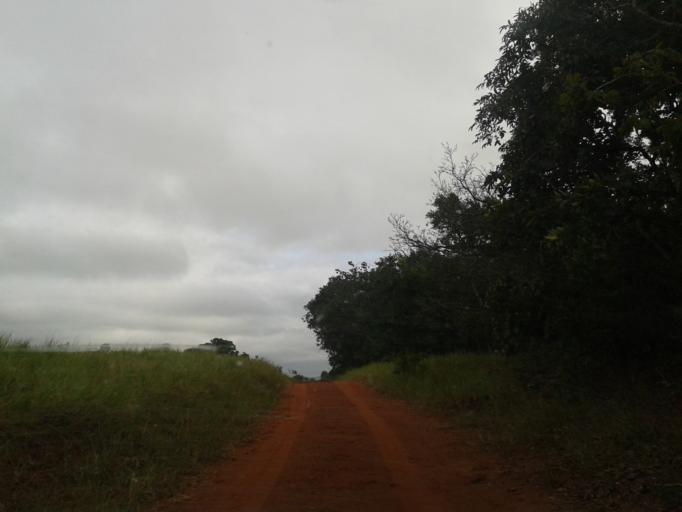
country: BR
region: Minas Gerais
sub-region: Campina Verde
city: Campina Verde
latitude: -19.4095
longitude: -49.6332
